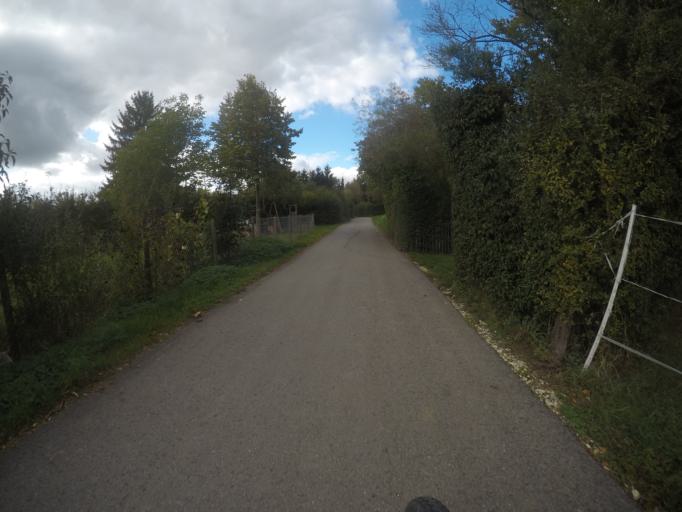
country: DE
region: Baden-Wuerttemberg
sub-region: Regierungsbezirk Stuttgart
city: Steinenbronn
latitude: 48.7329
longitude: 9.0951
